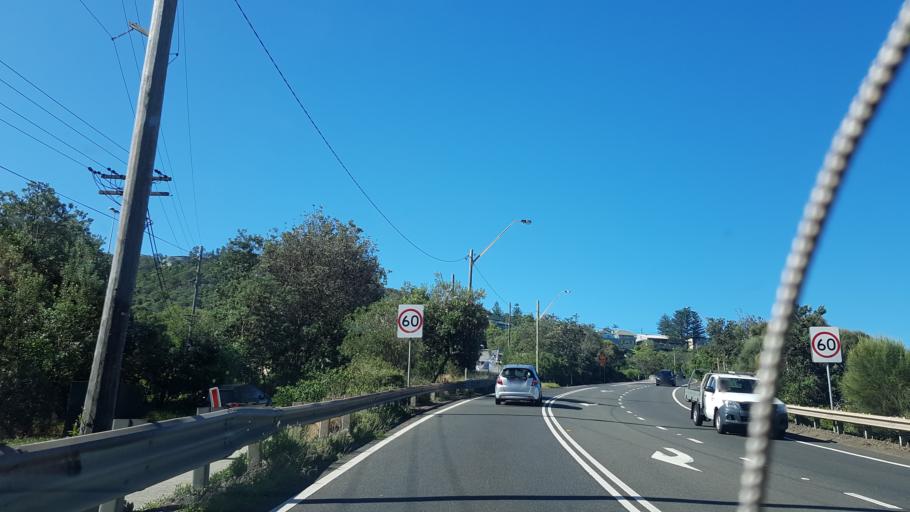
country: AU
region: New South Wales
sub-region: Pittwater
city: Newport
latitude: -33.6512
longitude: 151.3232
